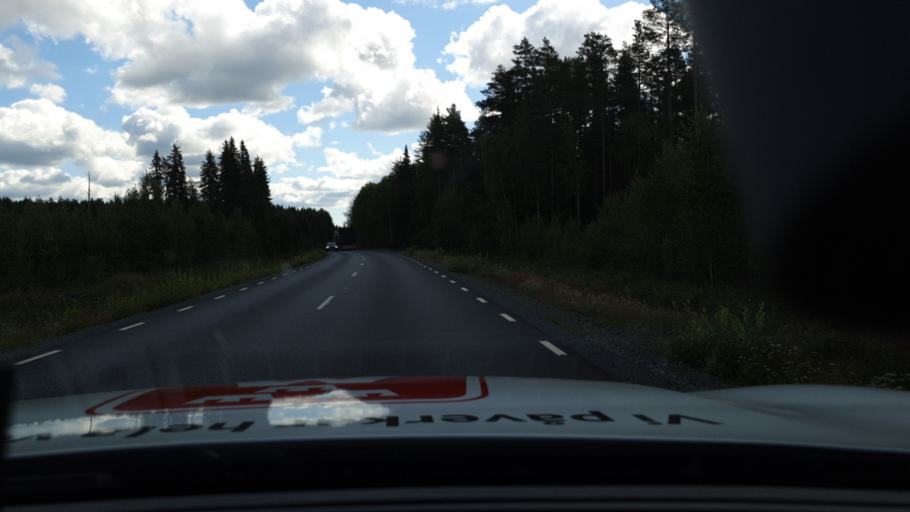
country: SE
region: Norrbotten
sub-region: Bodens Kommun
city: Saevast
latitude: 65.8394
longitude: 21.8199
